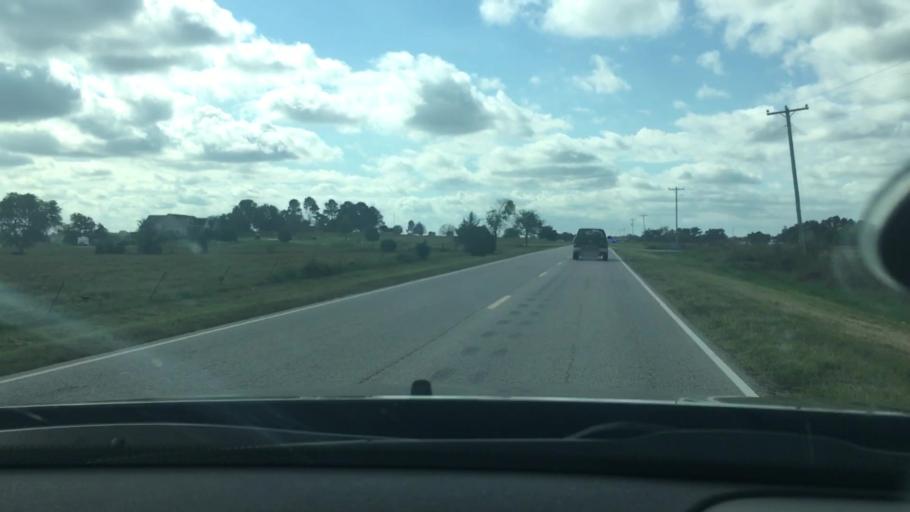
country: US
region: Oklahoma
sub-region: Pontotoc County
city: Ada
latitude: 34.7176
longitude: -96.6349
